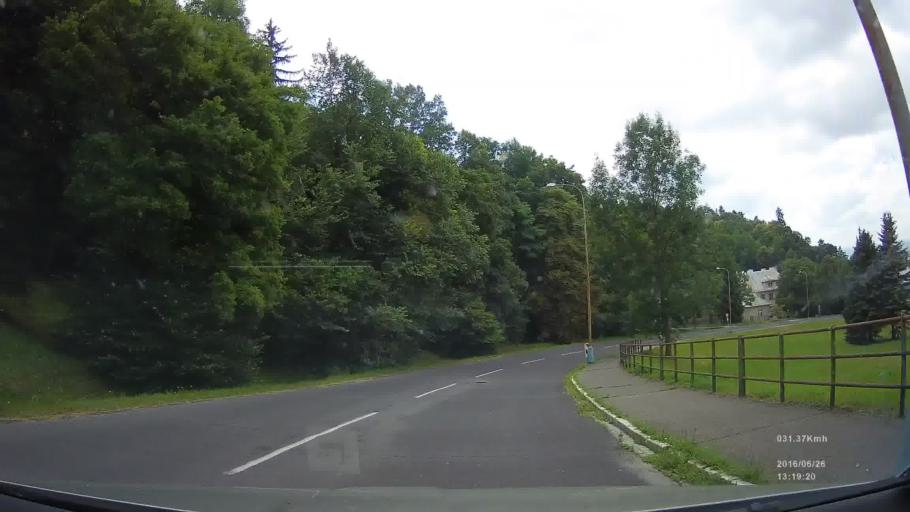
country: SK
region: Banskobystricky
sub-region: Okres Banska Bystrica
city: Zvolen
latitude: 48.6109
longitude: 19.1580
